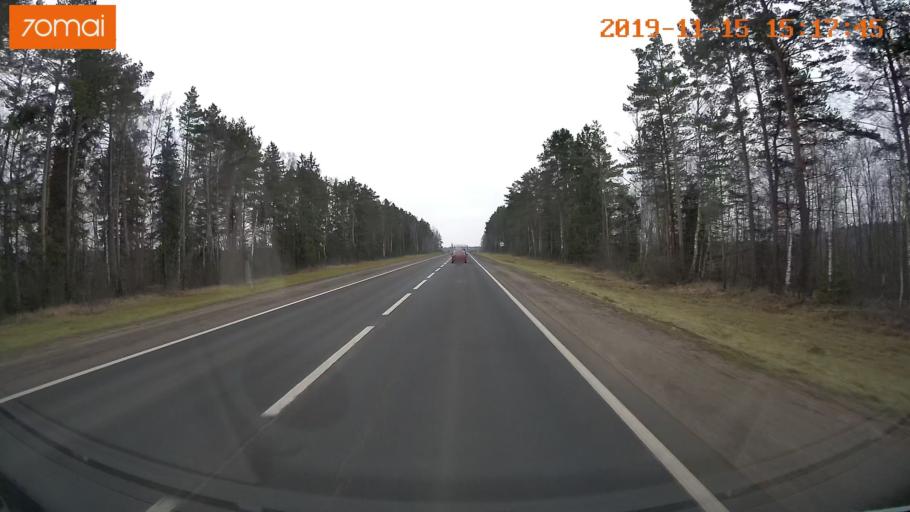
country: RU
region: Jaroslavl
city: Danilov
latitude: 58.2563
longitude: 40.1809
